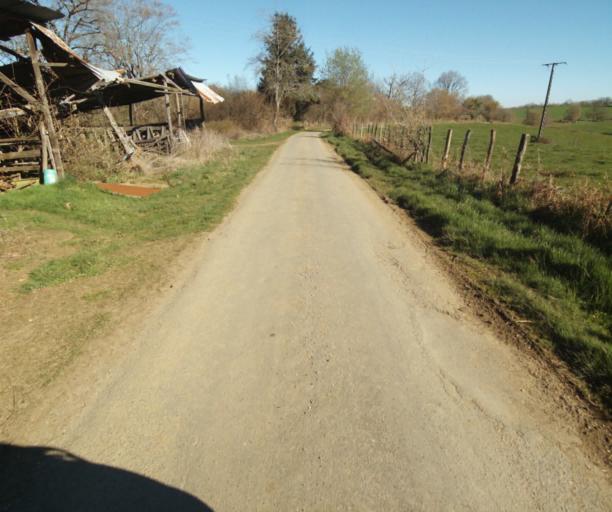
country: FR
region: Limousin
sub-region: Departement de la Correze
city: Chamboulive
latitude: 45.3998
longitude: 1.7085
